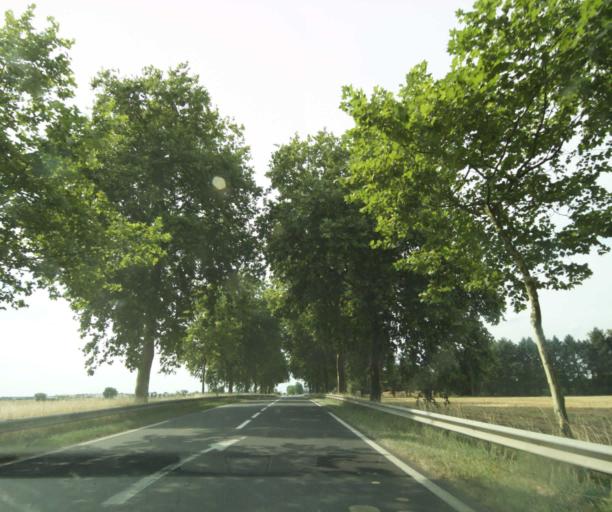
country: FR
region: Centre
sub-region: Departement d'Indre-et-Loire
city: Saint-Paterne-Racan
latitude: 47.5943
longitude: 0.5302
